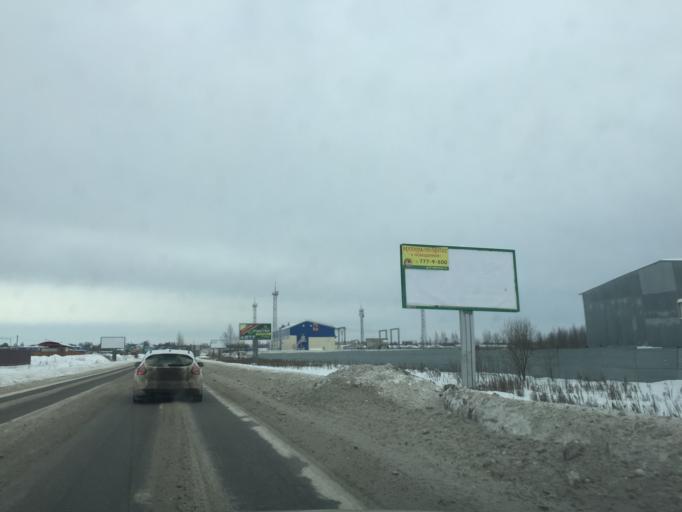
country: RU
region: Leningrad
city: Yanino Vtoroye
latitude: 59.9454
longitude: 30.5823
